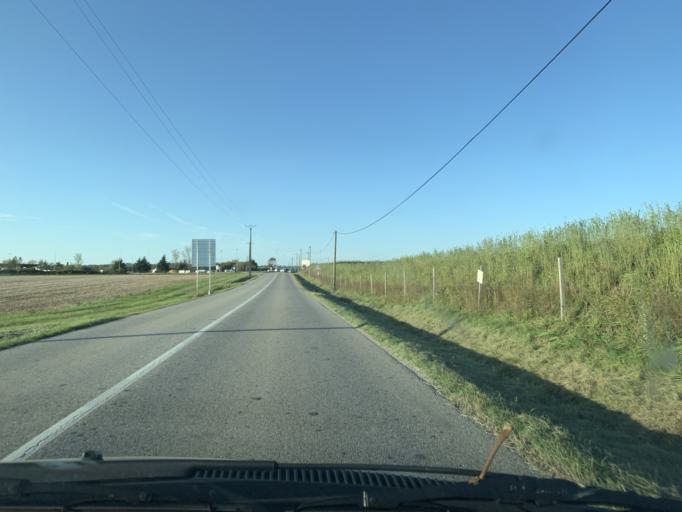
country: FR
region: Rhone-Alpes
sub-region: Departement de l'Ain
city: Saint-Maurice-de-Gourdans
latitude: 45.8581
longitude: 5.1843
